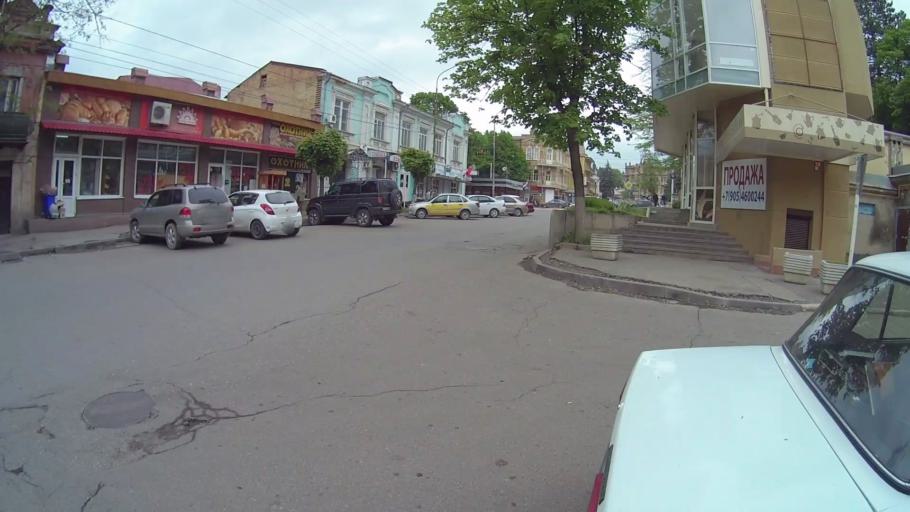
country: RU
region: Stavropol'skiy
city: Pyatigorsk
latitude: 44.0358
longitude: 43.0755
